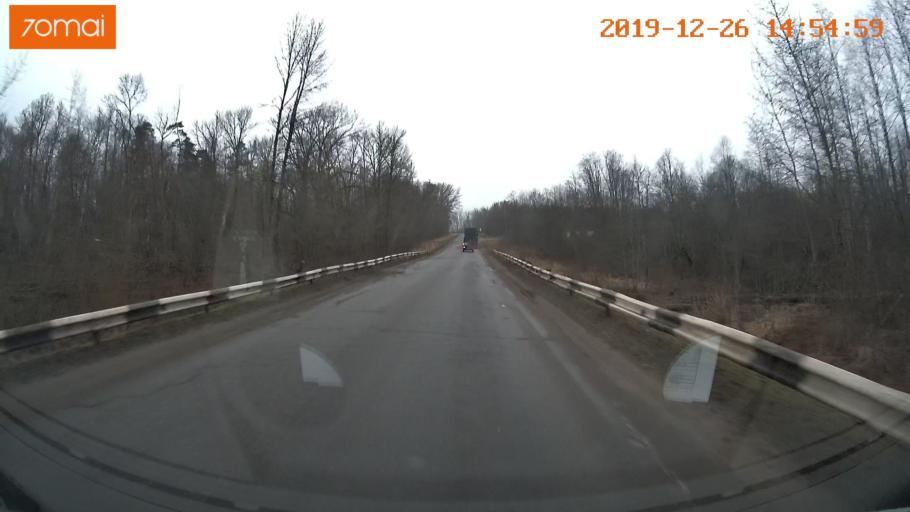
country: RU
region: Jaroslavl
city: Rybinsk
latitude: 58.3036
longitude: 38.8791
